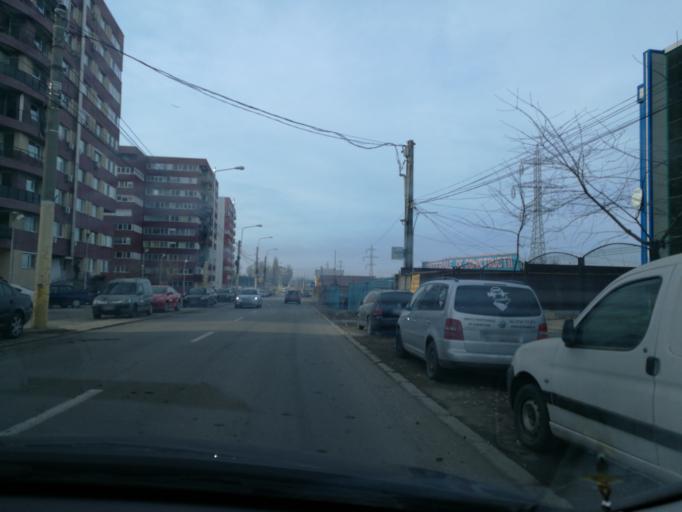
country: RO
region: Constanta
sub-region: Municipiul Constanta
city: Constanta
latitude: 44.1879
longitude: 28.6129
